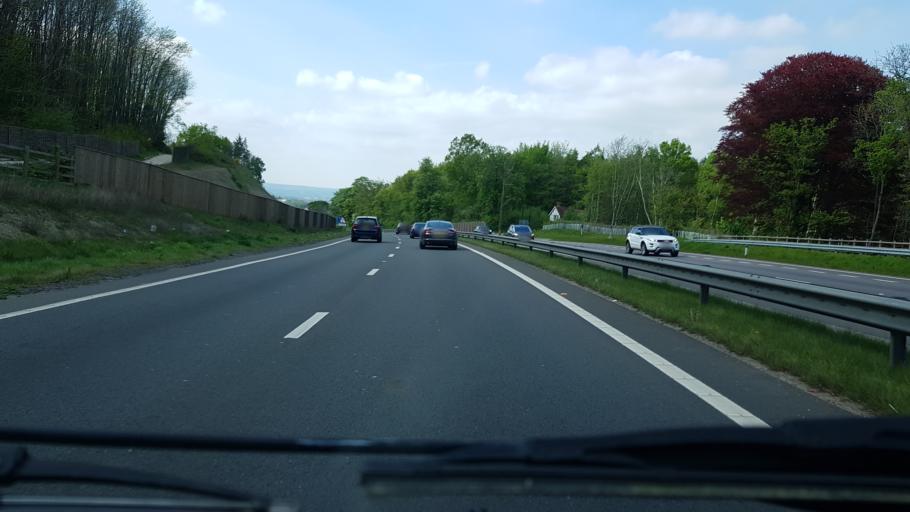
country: GB
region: England
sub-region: Kent
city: Tonbridge
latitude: 51.1731
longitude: 0.3007
